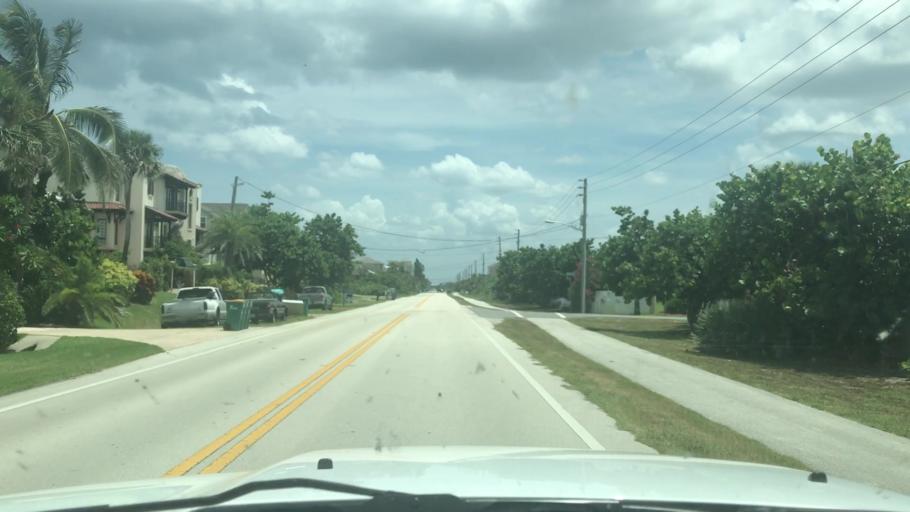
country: US
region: Florida
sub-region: Brevard County
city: Micco
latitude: 27.9324
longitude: -80.4887
